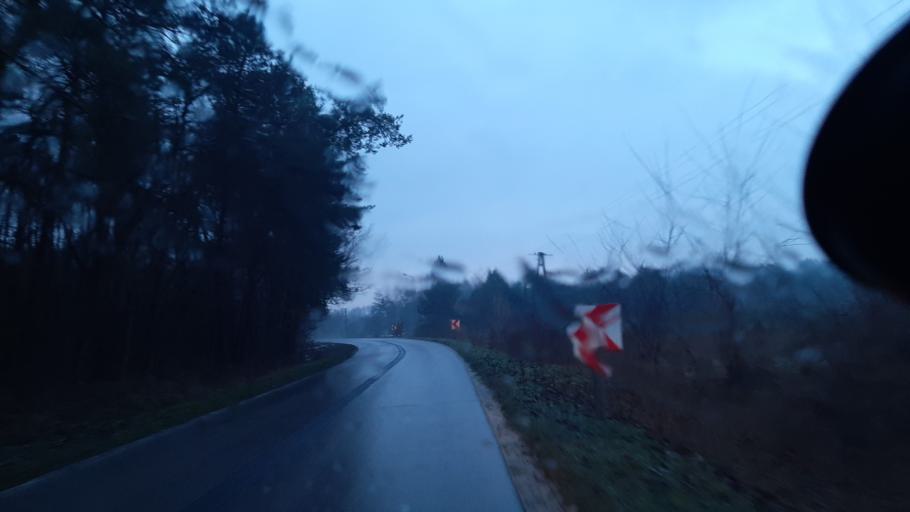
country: PL
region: Lublin Voivodeship
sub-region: Powiat lubartowski
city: Ostrowek
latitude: 51.5255
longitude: 22.5849
